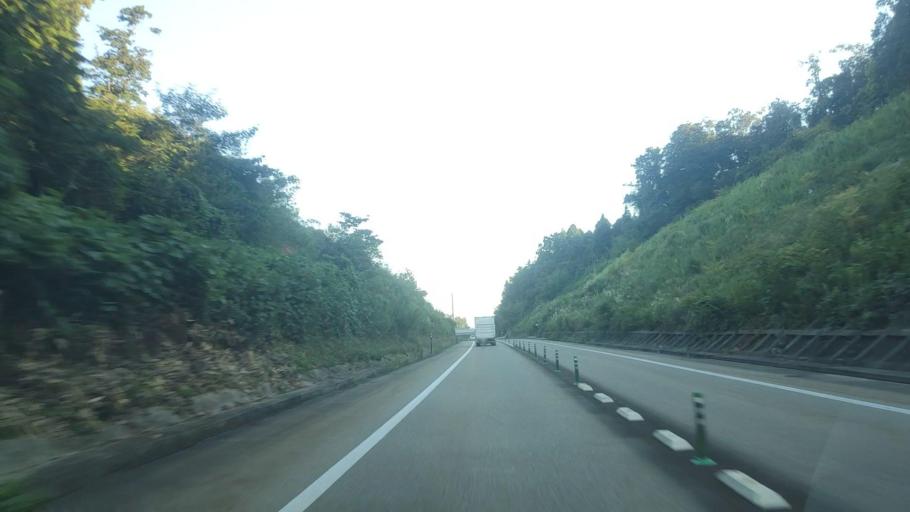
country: JP
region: Ishikawa
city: Nanao
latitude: 36.9967
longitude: 137.0442
